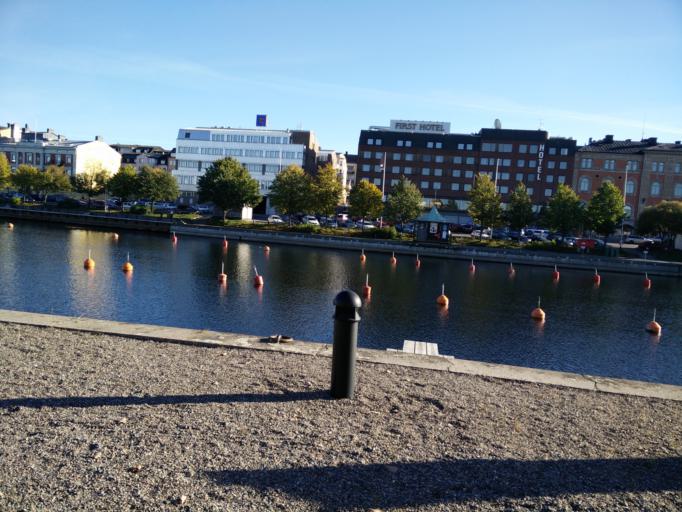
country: SE
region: Vaesternorrland
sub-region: Haernoesands Kommun
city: Haernoesand
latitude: 62.6346
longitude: 17.9367
